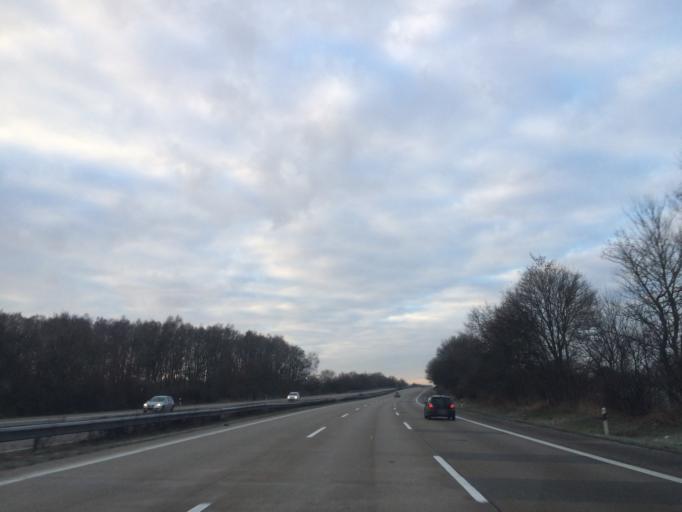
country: DE
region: Schleswig-Holstein
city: Stapelfeld
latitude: 53.6006
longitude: 10.2273
